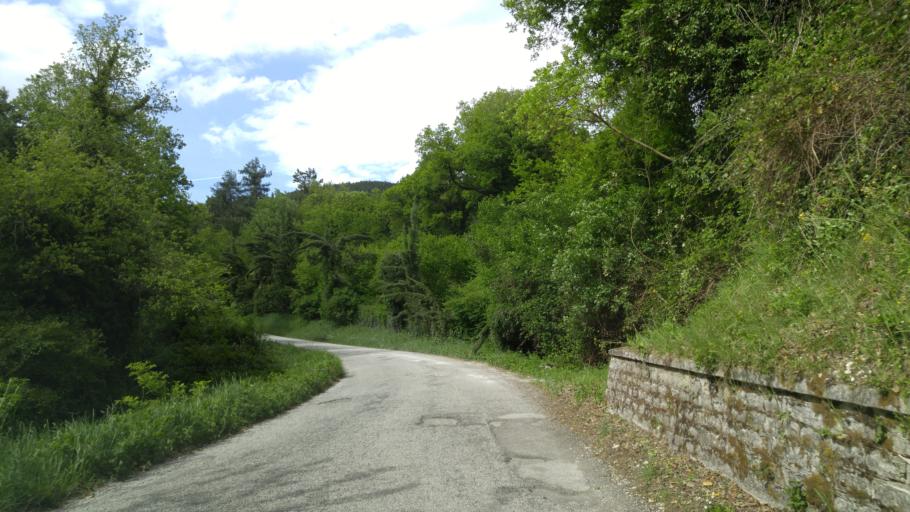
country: IT
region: The Marches
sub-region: Provincia di Pesaro e Urbino
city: Canavaccio
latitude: 43.7038
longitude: 12.7076
